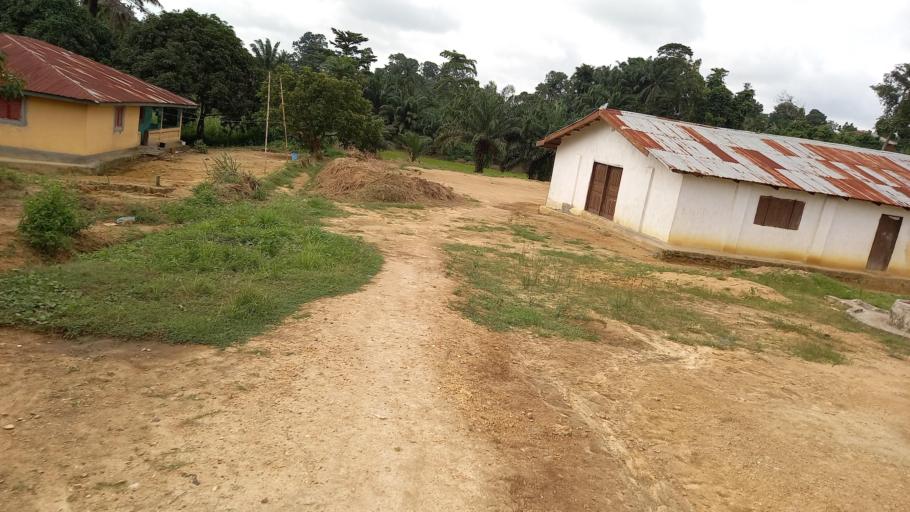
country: SL
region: Eastern Province
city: Kailahun
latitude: 8.2847
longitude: -10.5708
